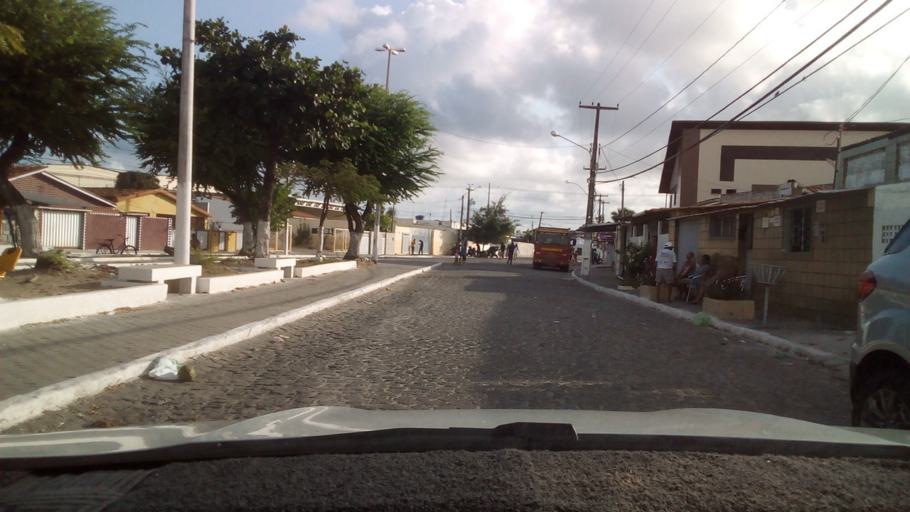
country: BR
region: Paraiba
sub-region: Cabedelo
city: Cabedelo
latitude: -6.9706
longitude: -34.8336
